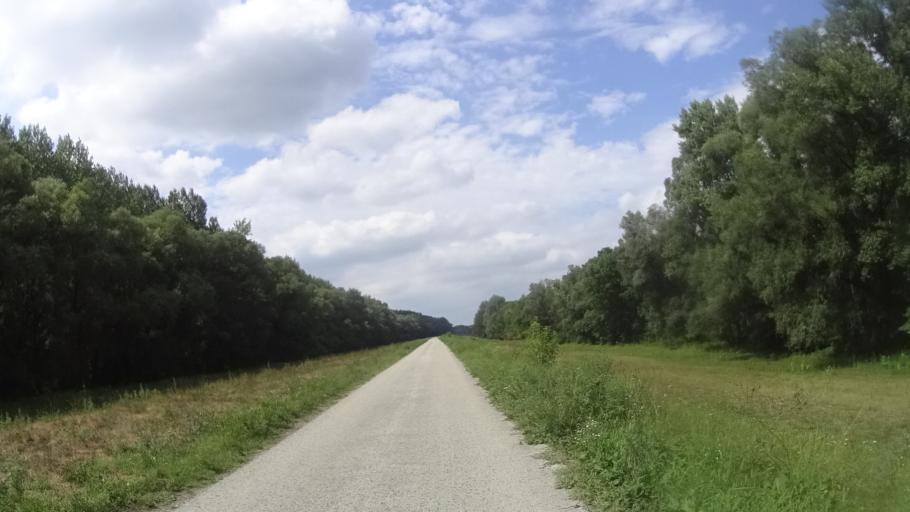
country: SK
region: Trnavsky
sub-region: Okres Dunajska Streda
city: Velky Meder
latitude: 47.7746
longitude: 17.7104
